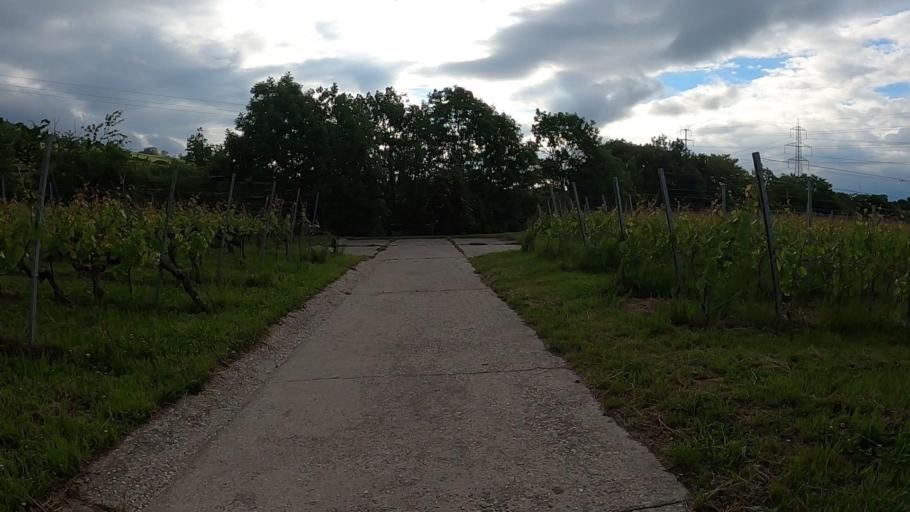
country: CH
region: Vaud
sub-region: Nyon District
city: Rolle
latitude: 46.4701
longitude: 6.3465
